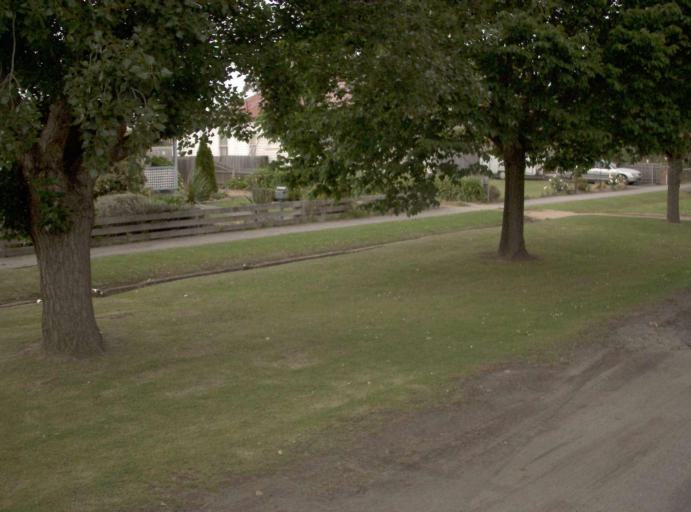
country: AU
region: Victoria
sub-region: Latrobe
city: Traralgon
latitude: -38.5676
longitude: 146.6751
